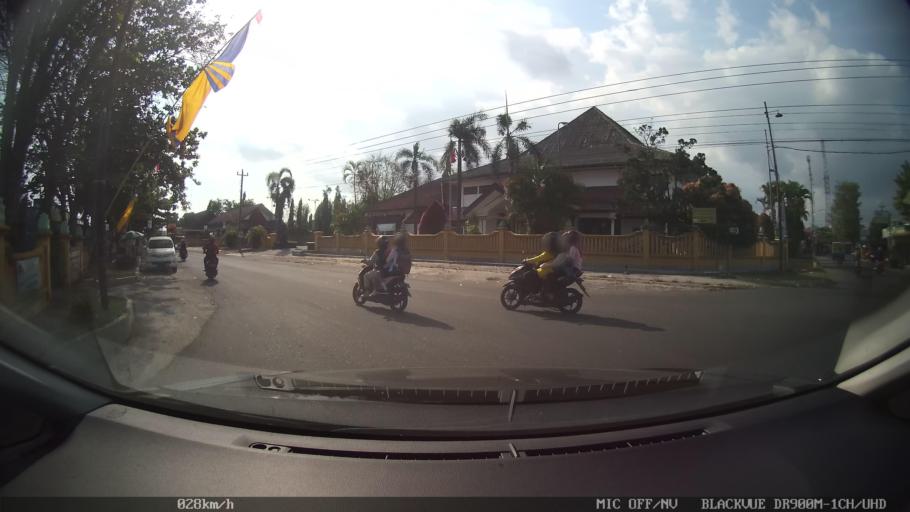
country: ID
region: Daerah Istimewa Yogyakarta
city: Kasihan
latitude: -7.8291
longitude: 110.3441
